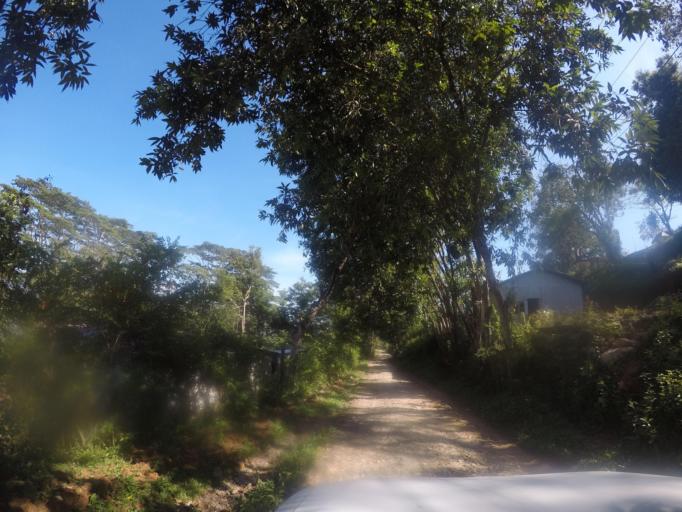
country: TL
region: Ermera
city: Gleno
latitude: -8.7301
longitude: 125.4375
